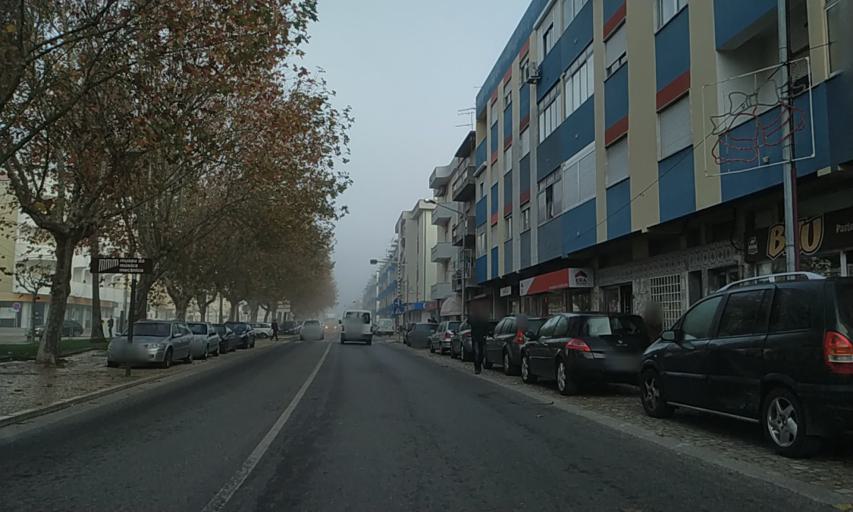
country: PT
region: Setubal
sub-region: Palmela
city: Pinhal Novo
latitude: 38.6318
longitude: -8.9144
